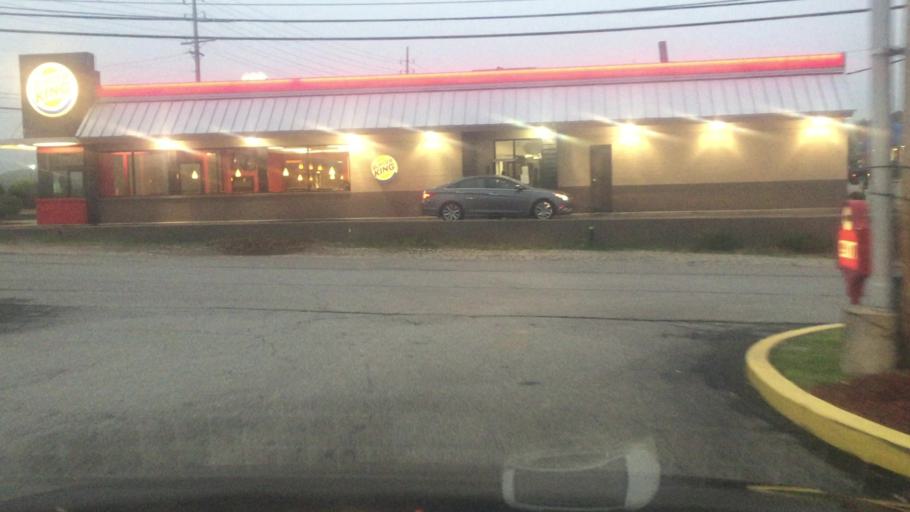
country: US
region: Missouri
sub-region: Warren County
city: Warrenton
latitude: 38.8222
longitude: -91.1379
